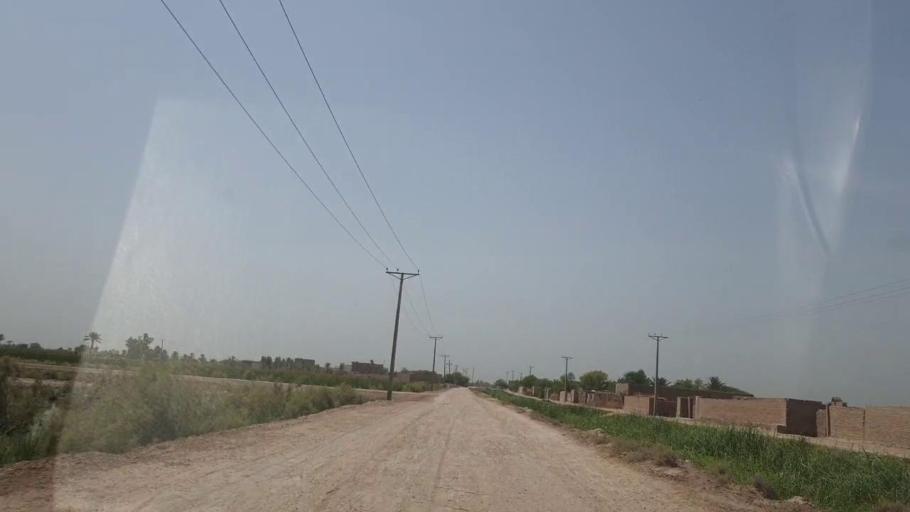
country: PK
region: Sindh
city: Ranipur
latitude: 27.2985
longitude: 68.5454
